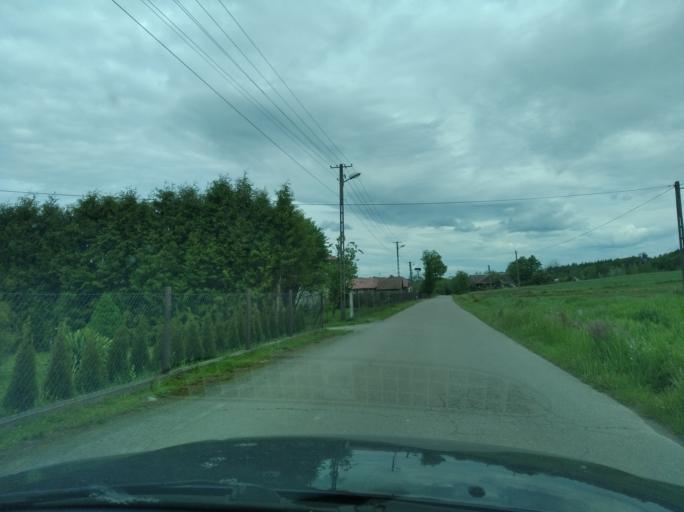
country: PL
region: Subcarpathian Voivodeship
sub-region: Powiat przeworski
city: Jawornik Polski
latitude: 49.8357
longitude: 22.3025
